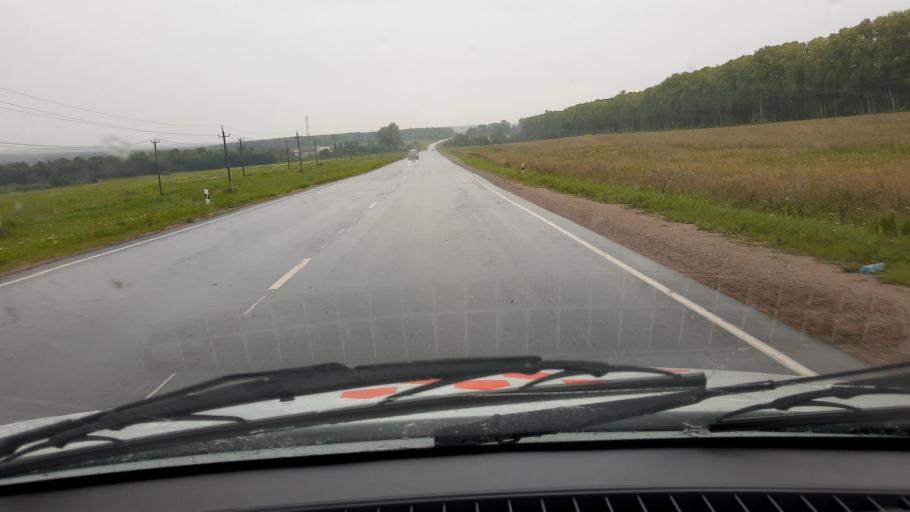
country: RU
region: Bashkortostan
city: Iglino
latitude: 54.8749
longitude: 56.4694
